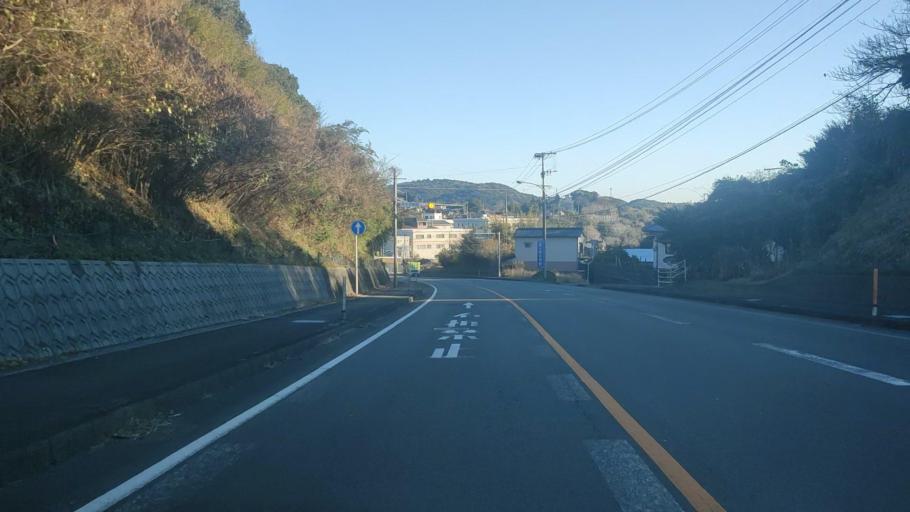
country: JP
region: Miyazaki
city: Takanabe
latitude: 32.3285
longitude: 131.6023
